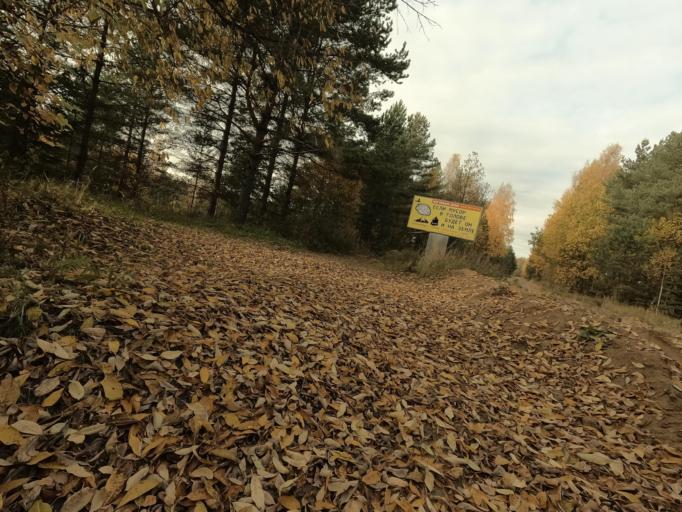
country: RU
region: Leningrad
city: Priladozhskiy
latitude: 59.6742
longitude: 31.3665
